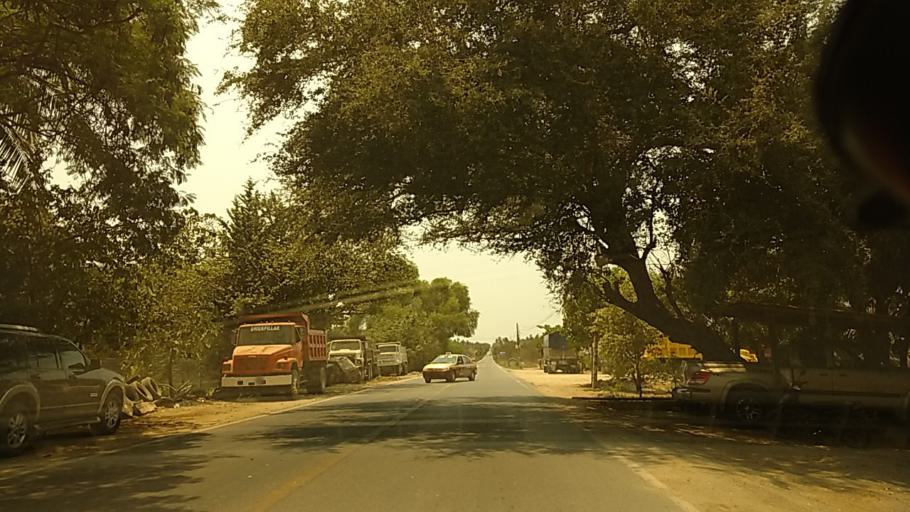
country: MX
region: Guerrero
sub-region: Tecpan de Galeana
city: Villa Rotaria
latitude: 17.2713
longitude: -100.8968
